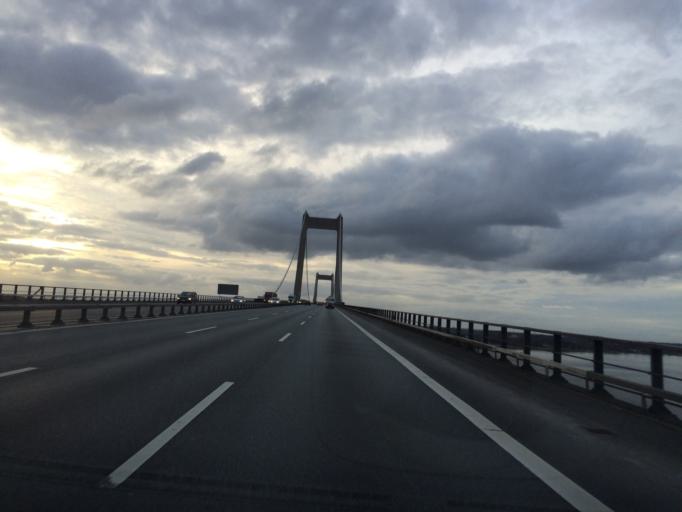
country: DK
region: South Denmark
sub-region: Middelfart Kommune
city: Strib
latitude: 55.5163
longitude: 9.7609
